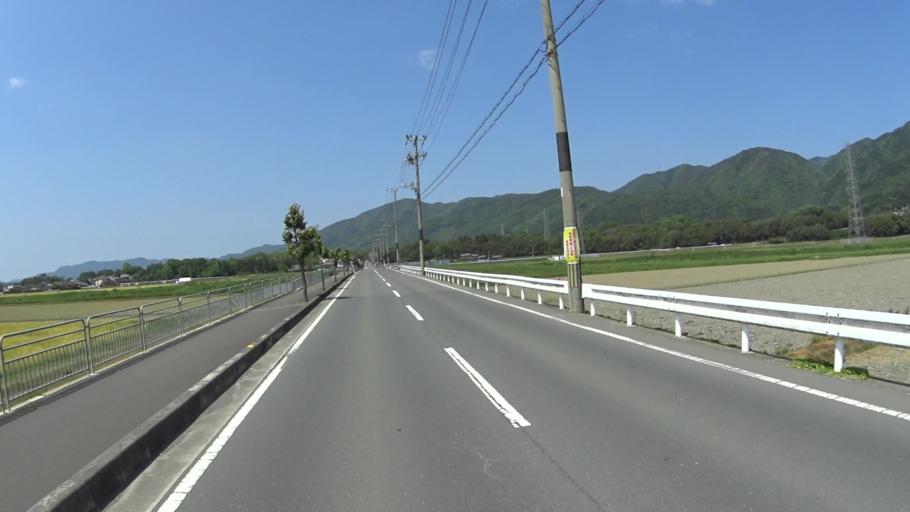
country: JP
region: Kyoto
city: Kameoka
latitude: 35.0353
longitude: 135.5746
